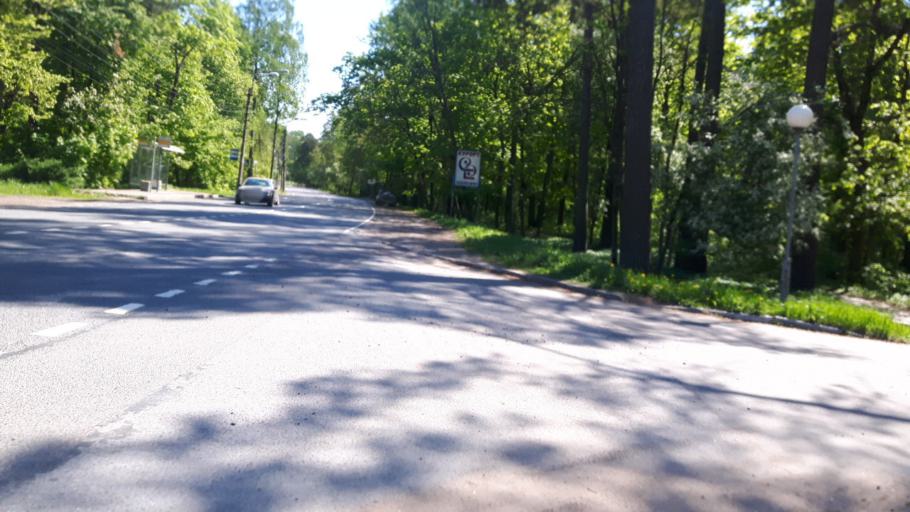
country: RU
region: St.-Petersburg
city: Zelenogorsk
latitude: 60.1937
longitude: 29.6689
